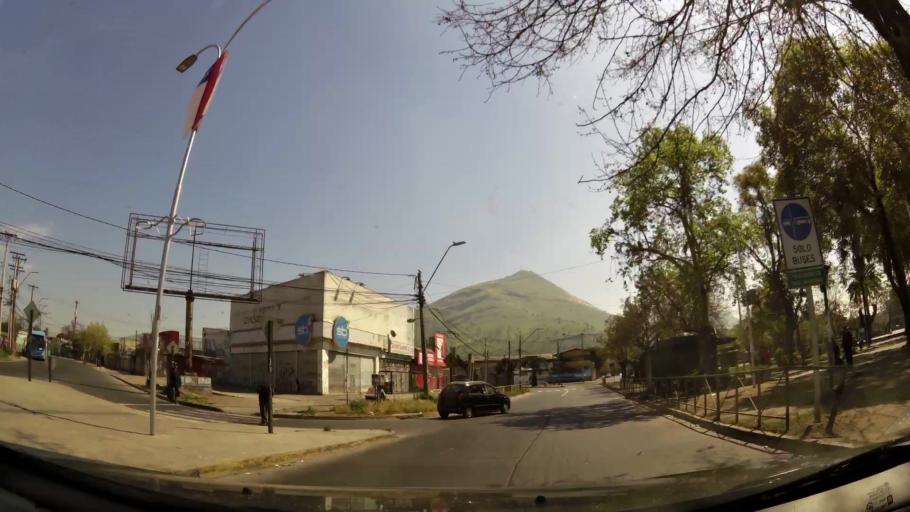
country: CL
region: Santiago Metropolitan
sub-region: Provincia de Santiago
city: Lo Prado
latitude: -33.4046
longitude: -70.7055
